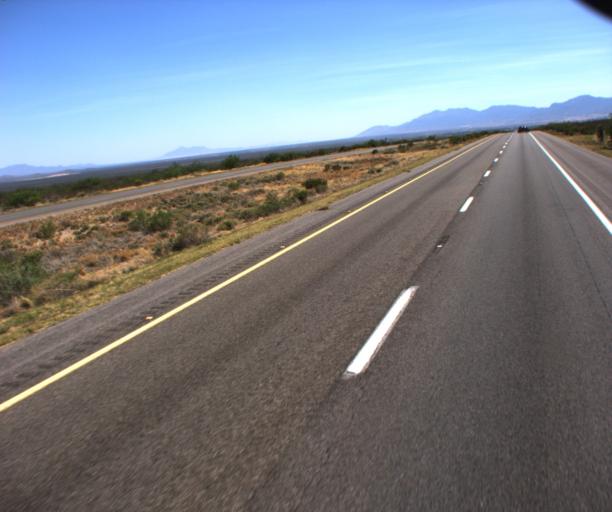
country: US
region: Arizona
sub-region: Cochise County
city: Huachuca City
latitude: 31.7776
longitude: -110.3503
